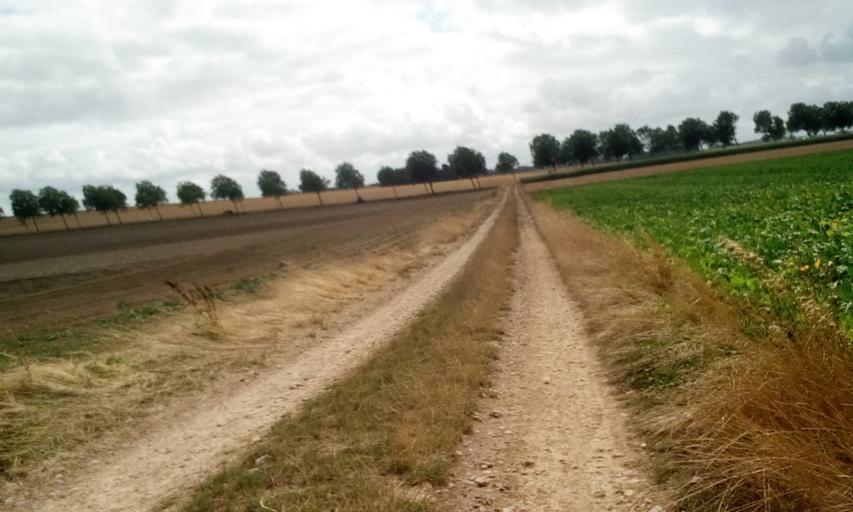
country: FR
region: Lower Normandy
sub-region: Departement du Calvados
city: Cheux
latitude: 49.1763
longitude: -0.5432
